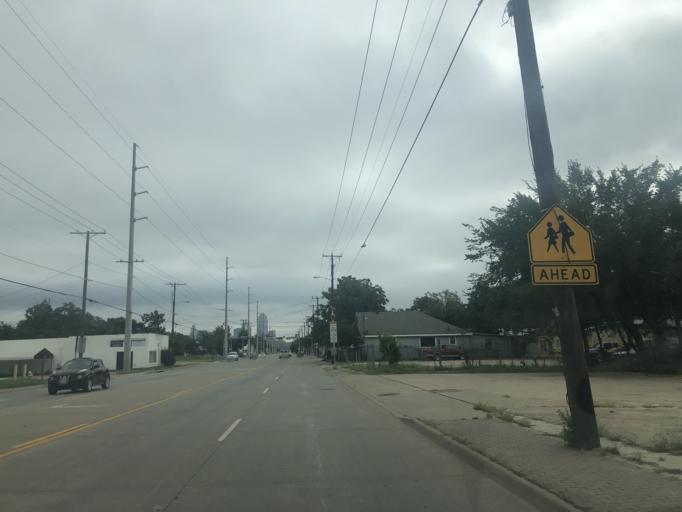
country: US
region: Texas
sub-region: Dallas County
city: Dallas
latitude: 32.7785
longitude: -96.8499
